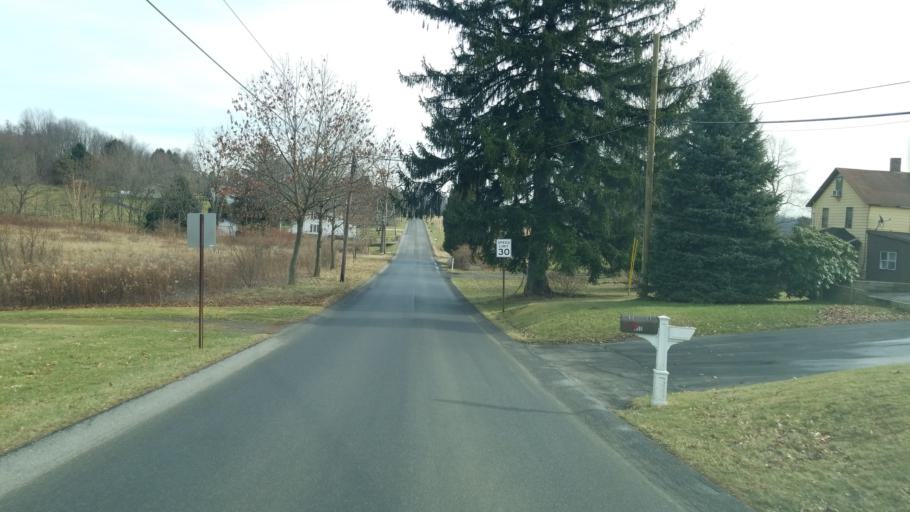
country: US
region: Pennsylvania
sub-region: Indiana County
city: Chevy Chase Heights
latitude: 40.6417
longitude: -79.1299
